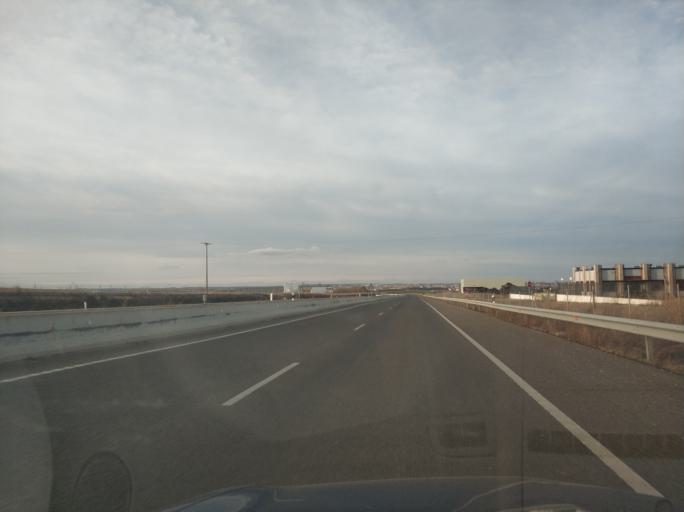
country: ES
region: Castille and Leon
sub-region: Provincia de Zamora
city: Morales del Vino
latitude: 41.4612
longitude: -5.7329
